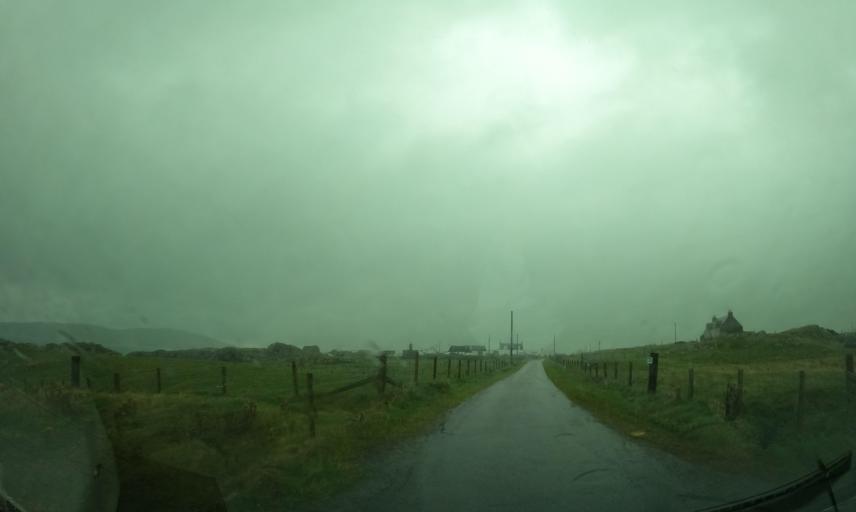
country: GB
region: Scotland
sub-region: Eilean Siar
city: Barra
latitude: 56.4540
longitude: -6.9401
